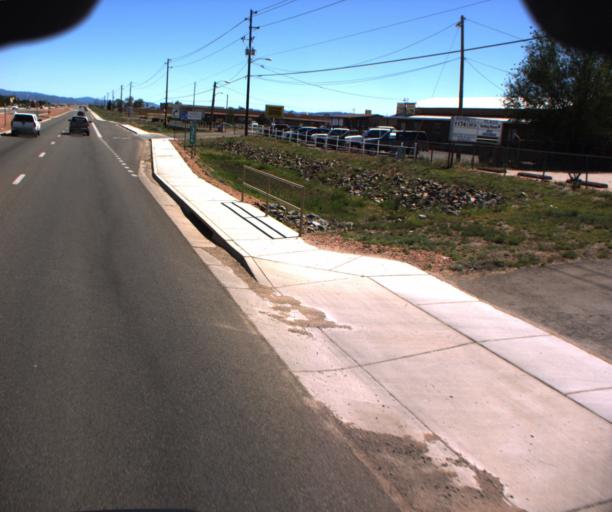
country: US
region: Arizona
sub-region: Yavapai County
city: Chino Valley
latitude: 34.7286
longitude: -112.4541
